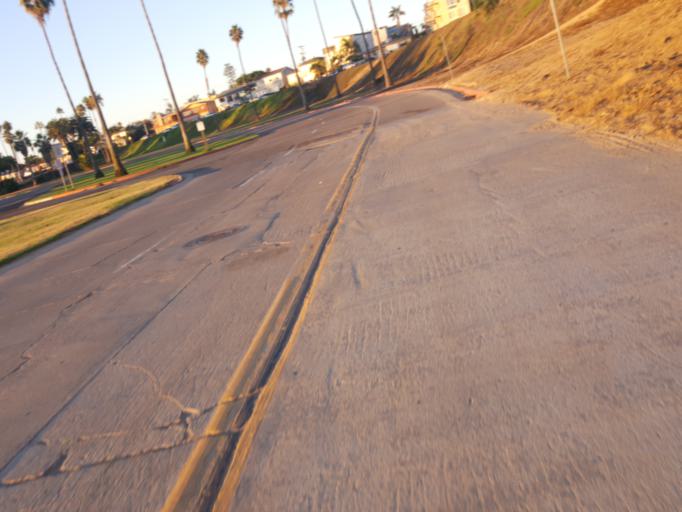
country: US
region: California
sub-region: San Diego County
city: La Jolla
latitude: 32.7894
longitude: -117.2334
